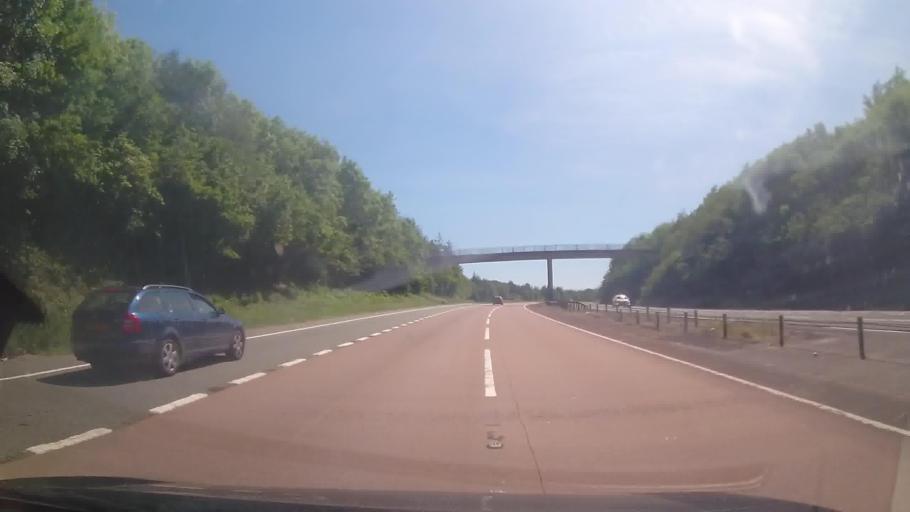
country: GB
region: England
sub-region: Devon
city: Ottery St Mary
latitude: 50.7553
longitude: -3.3287
